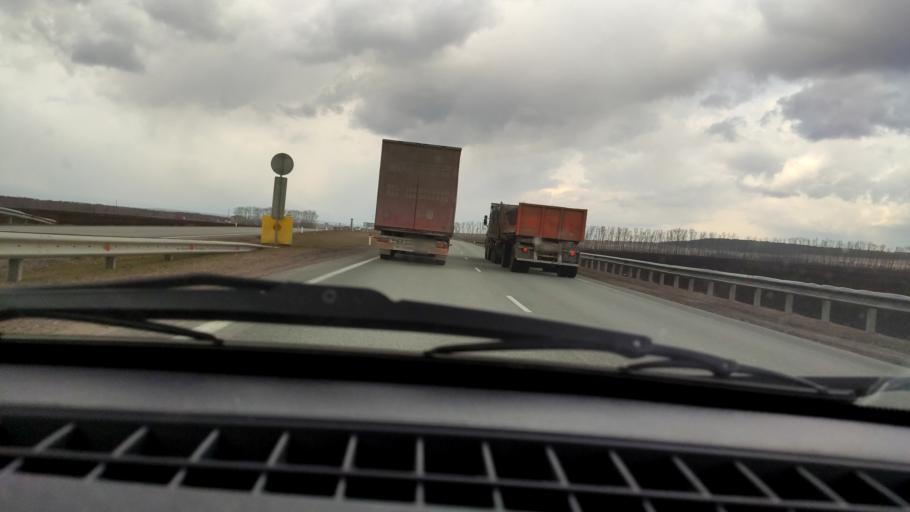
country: RU
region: Bashkortostan
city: Asanovo
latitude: 54.9511
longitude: 55.5832
